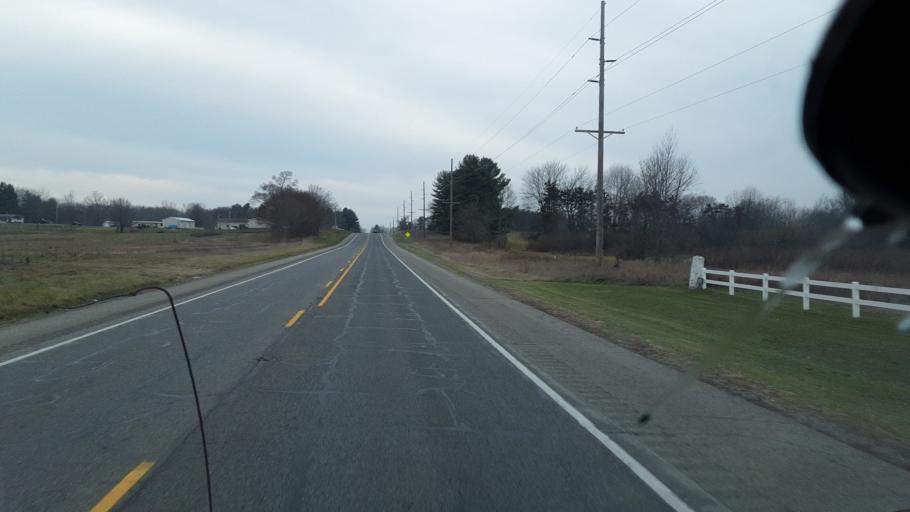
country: US
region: Indiana
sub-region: Steuben County
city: Angola
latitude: 41.6439
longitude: -85.1838
